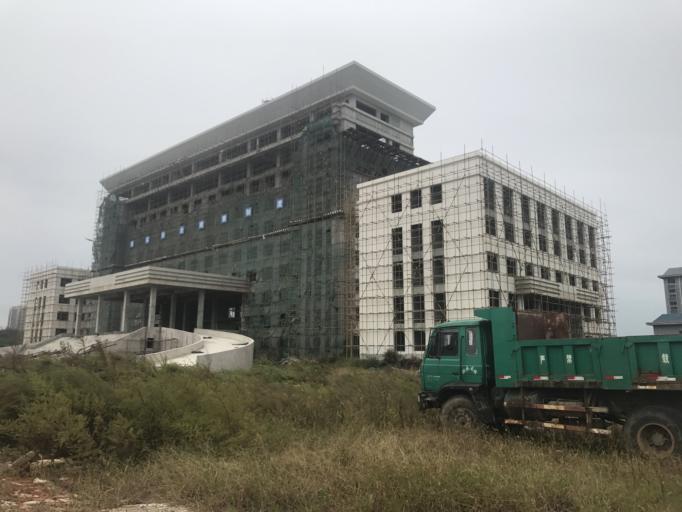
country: CN
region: Hubei
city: Anlu
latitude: 31.2644
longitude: 113.7153
